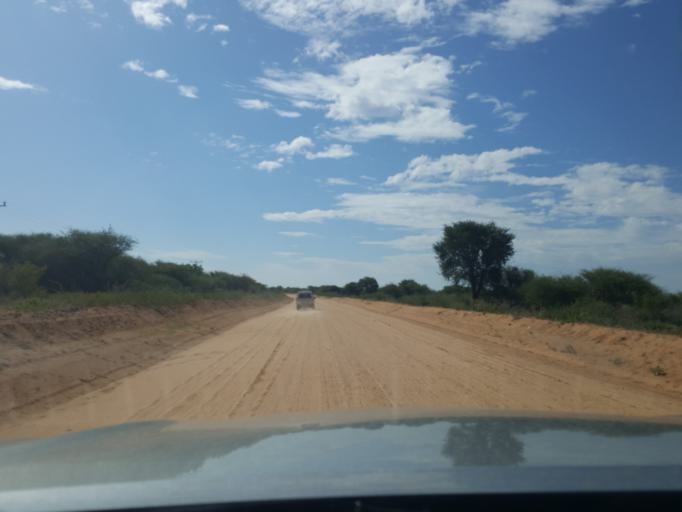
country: BW
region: Kweneng
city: Khudumelapye
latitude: -23.8155
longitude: 24.8229
